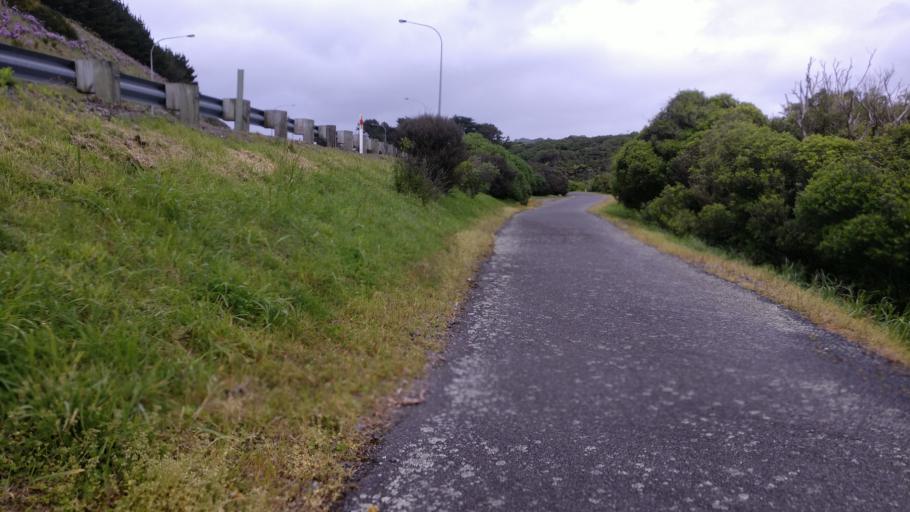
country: NZ
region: Wellington
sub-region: Porirua City
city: Porirua
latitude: -41.0489
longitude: 174.8774
